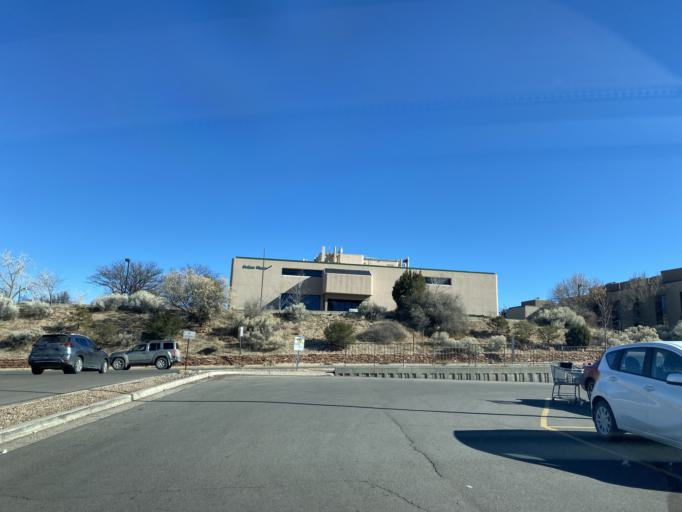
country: US
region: New Mexico
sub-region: Santa Fe County
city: Santa Fe
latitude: 35.6585
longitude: -105.9596
